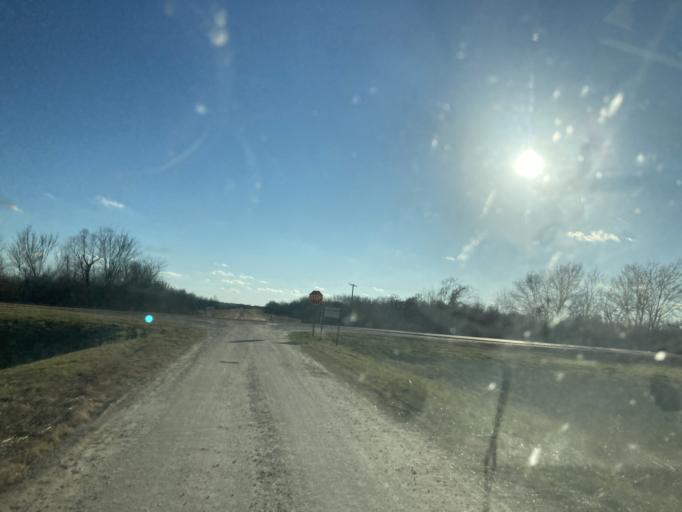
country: US
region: Mississippi
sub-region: Yazoo County
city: Yazoo City
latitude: 32.9174
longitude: -90.5544
